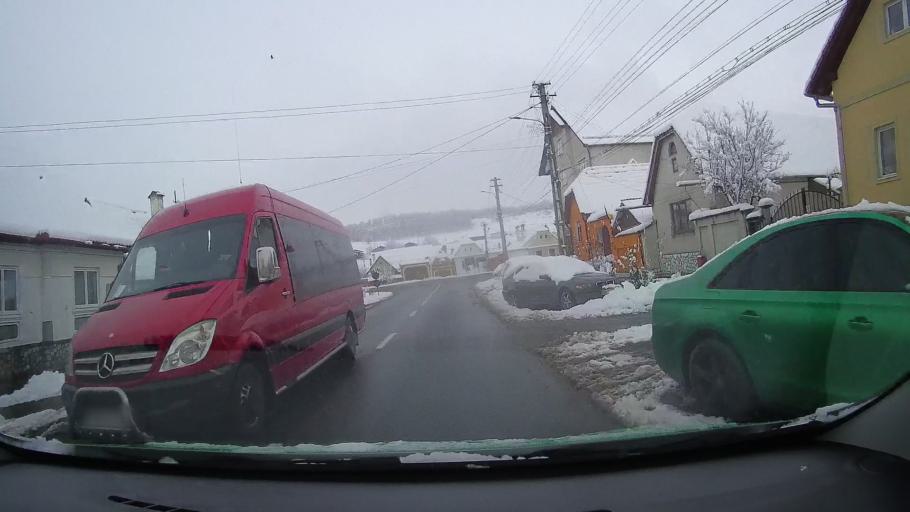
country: RO
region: Sibiu
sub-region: Comuna Cristian
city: Cristian
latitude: 45.7881
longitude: 24.0309
